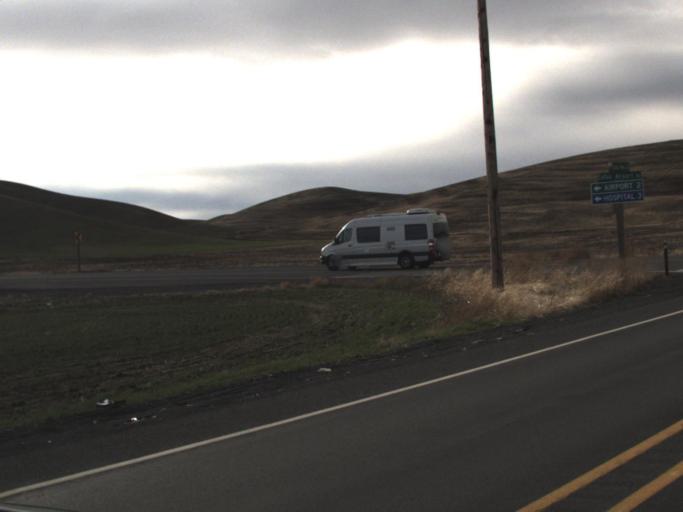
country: US
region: Washington
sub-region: Whitman County
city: Colfax
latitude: 46.8644
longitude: -117.4365
